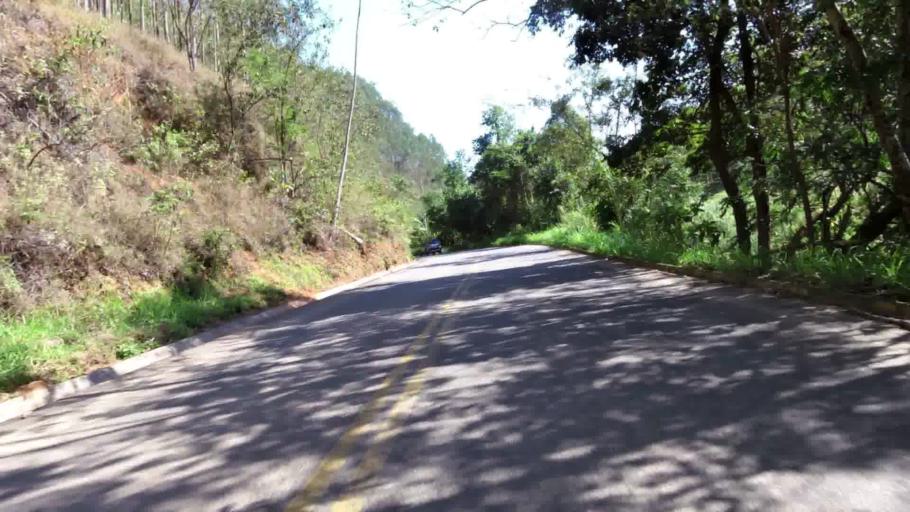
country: BR
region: Espirito Santo
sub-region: Alfredo Chaves
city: Alfredo Chaves
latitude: -20.5916
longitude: -40.7933
